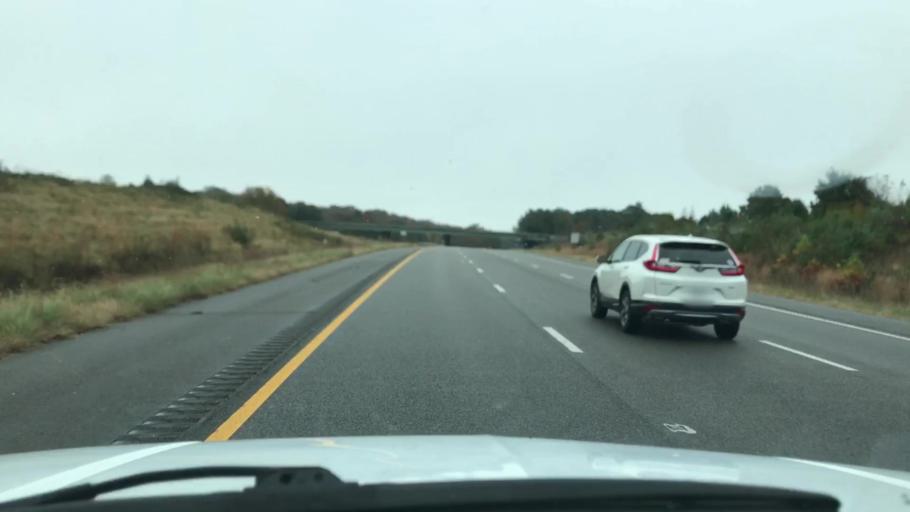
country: US
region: Virginia
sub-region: Henrico County
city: Glen Allen
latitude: 37.6817
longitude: -77.5261
